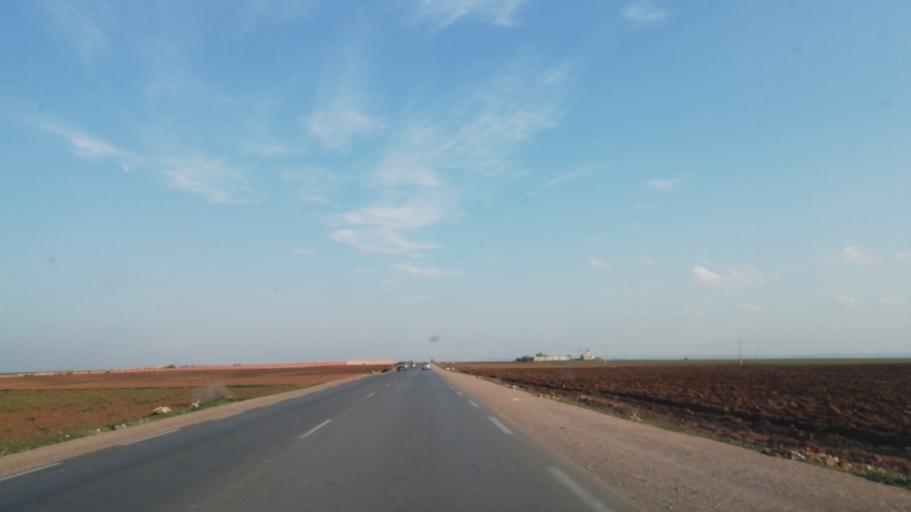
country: DZ
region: Relizane
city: Relizane
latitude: 35.8939
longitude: 0.6092
